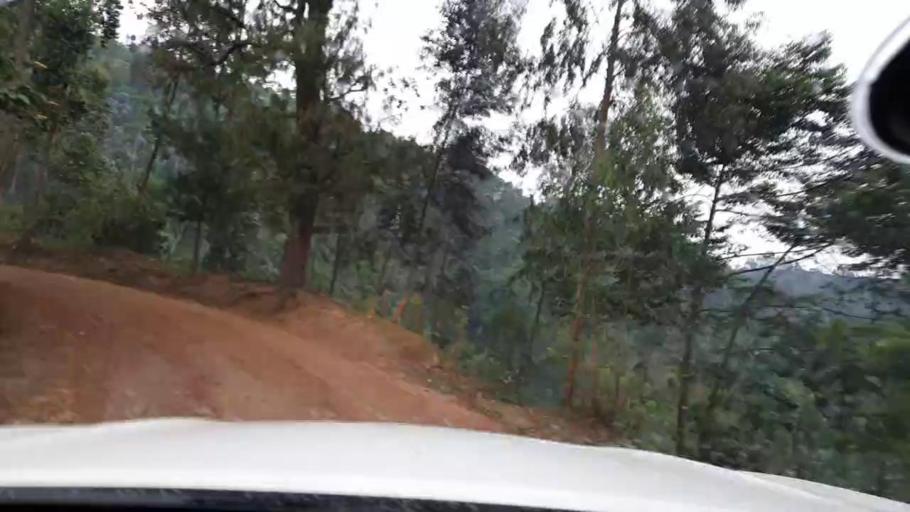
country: RW
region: Western Province
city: Cyangugu
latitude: -2.4098
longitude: 29.1885
